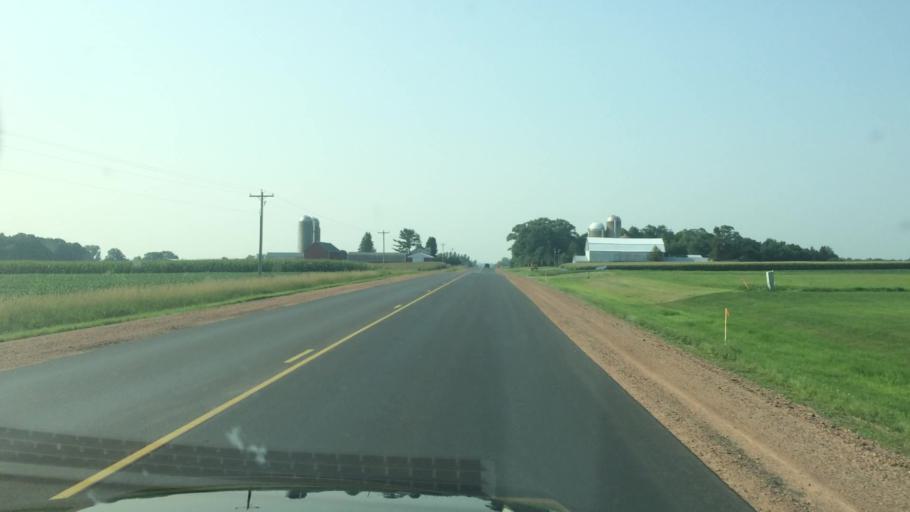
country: US
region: Wisconsin
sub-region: Marathon County
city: Stratford
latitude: 44.8553
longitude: -90.0792
